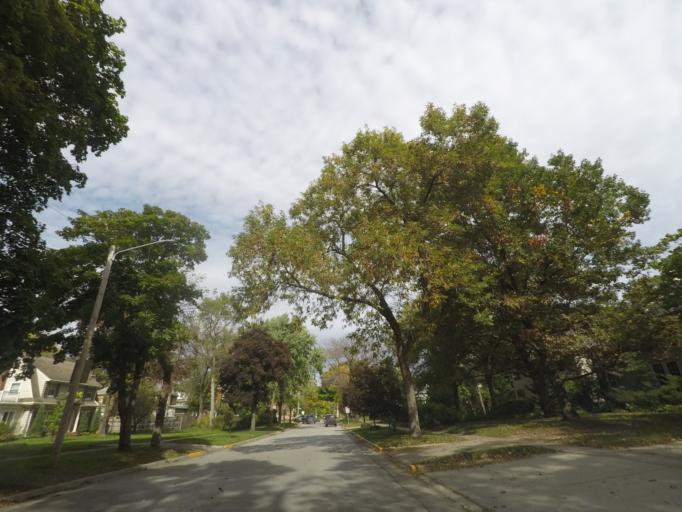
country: US
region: Iowa
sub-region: Story County
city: Ames
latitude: 42.0183
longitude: -93.6443
